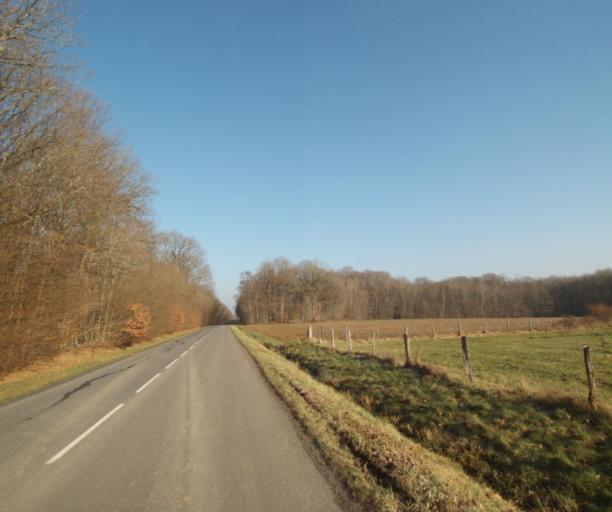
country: FR
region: Champagne-Ardenne
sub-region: Departement de la Haute-Marne
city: Laneuville-a-Remy
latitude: 48.4660
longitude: 4.9137
